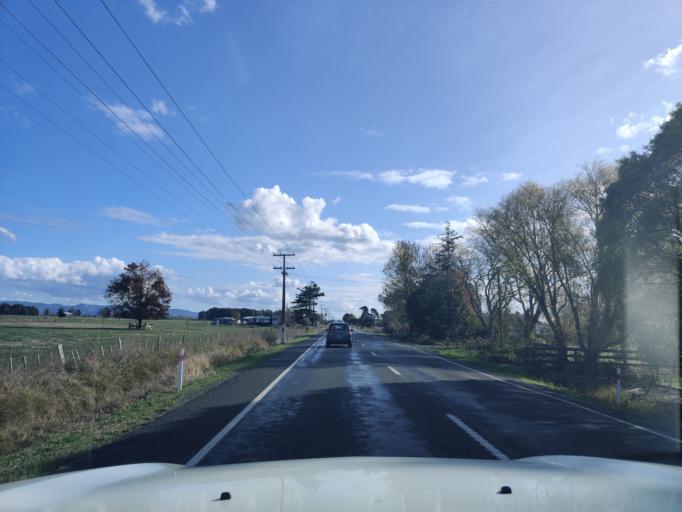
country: NZ
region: Waikato
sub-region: Hauraki District
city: Ngatea
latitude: -37.3114
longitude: 175.5772
